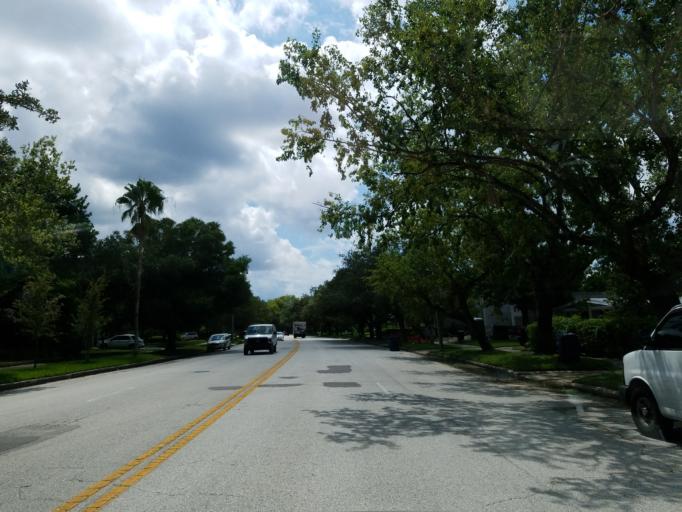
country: US
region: Florida
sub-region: Hillsborough County
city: Tampa
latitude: 27.9273
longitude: -82.4580
